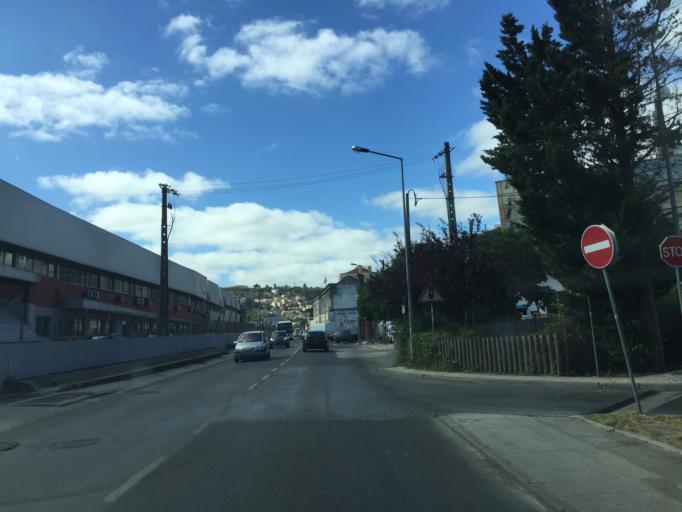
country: PT
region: Lisbon
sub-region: Odivelas
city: Povoa de Santo Adriao
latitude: 38.8051
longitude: -9.1576
